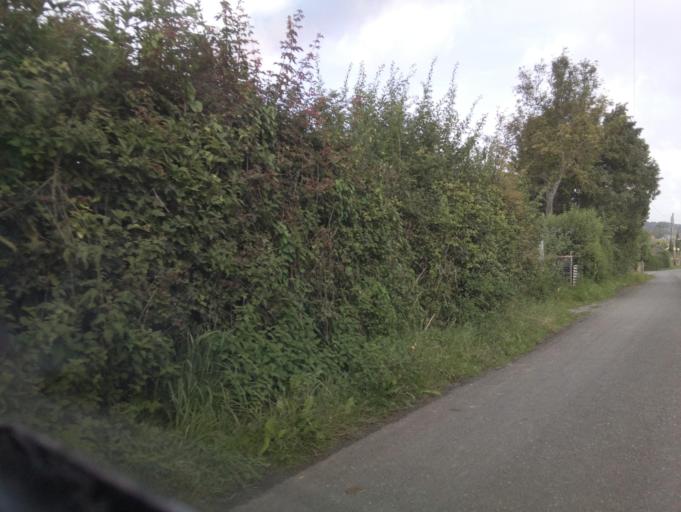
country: GB
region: England
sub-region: Somerset
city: Evercreech
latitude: 51.1489
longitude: -2.4921
